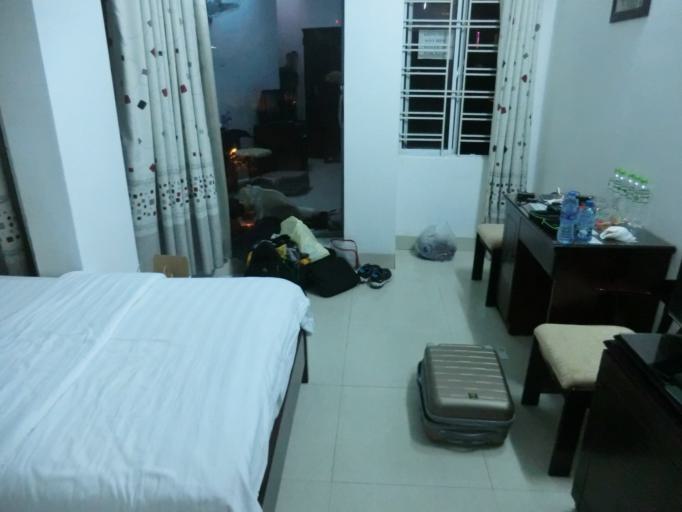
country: VN
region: Da Nang
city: Da Nang
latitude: 16.0678
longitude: 108.2222
